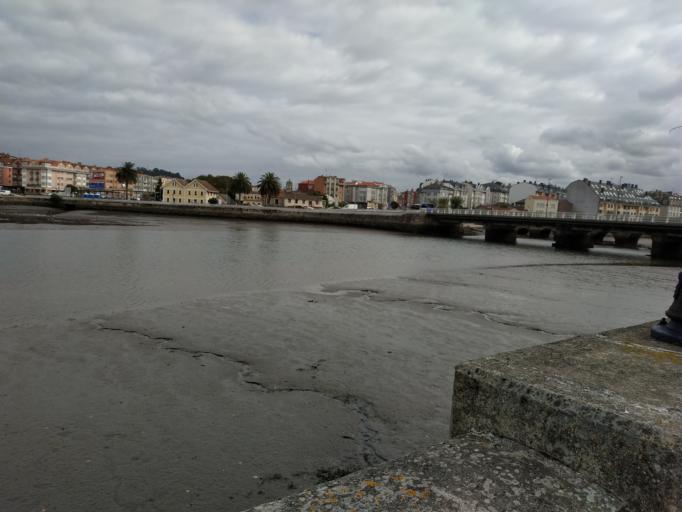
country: ES
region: Galicia
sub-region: Provincia da Coruna
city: Cambre
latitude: 43.3165
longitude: -8.3607
